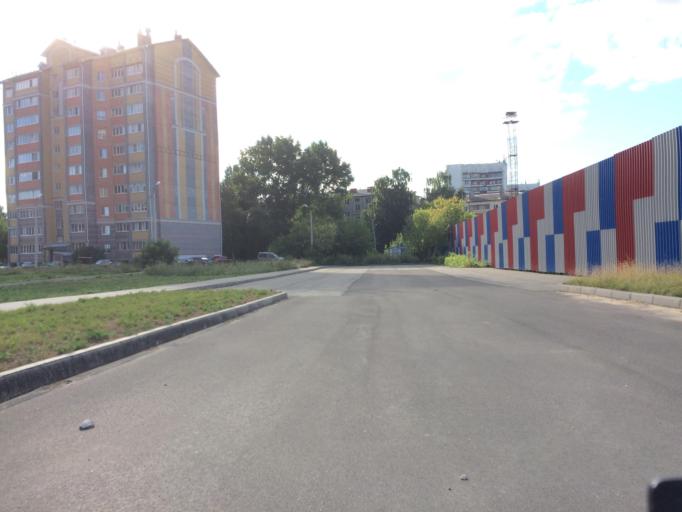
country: RU
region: Mariy-El
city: Yoshkar-Ola
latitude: 56.6244
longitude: 47.8783
